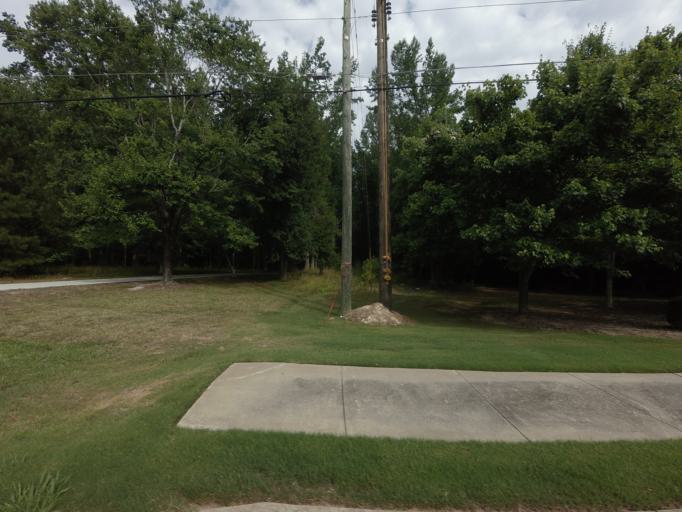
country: US
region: Georgia
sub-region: Gwinnett County
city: Duluth
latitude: 34.0490
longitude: -84.1354
